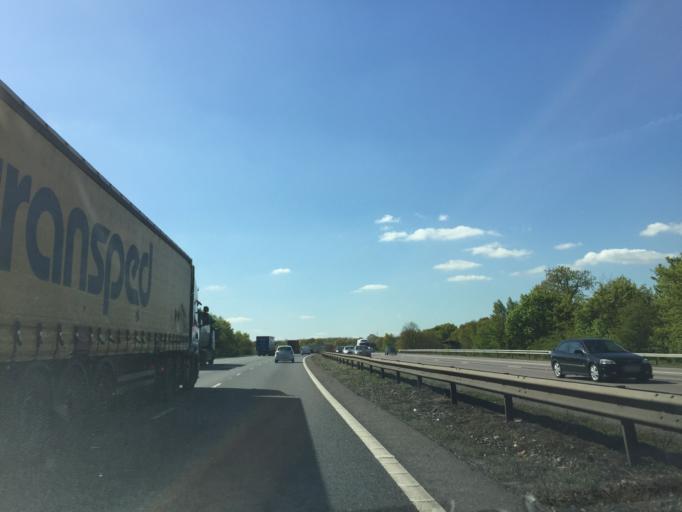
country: GB
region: England
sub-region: Essex
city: Epping
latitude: 51.7087
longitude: 0.1462
